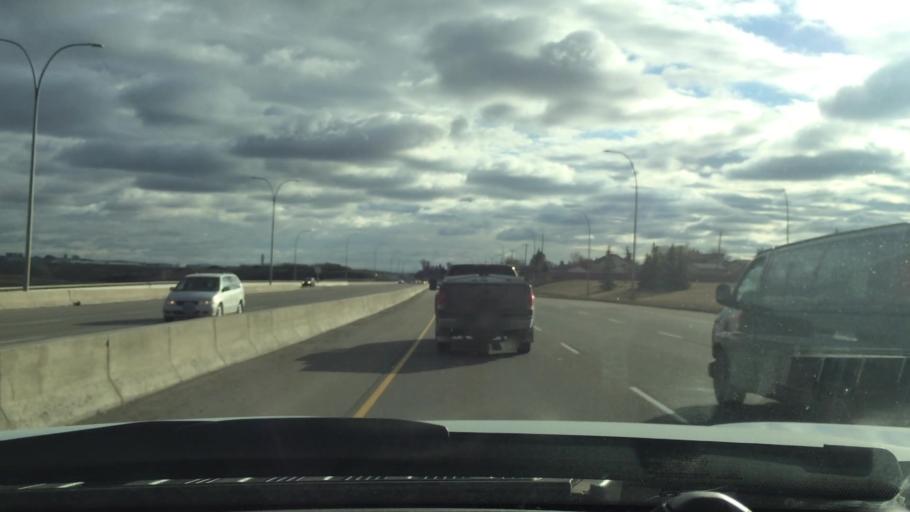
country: CA
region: Alberta
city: Calgary
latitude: 51.1335
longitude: -114.0698
